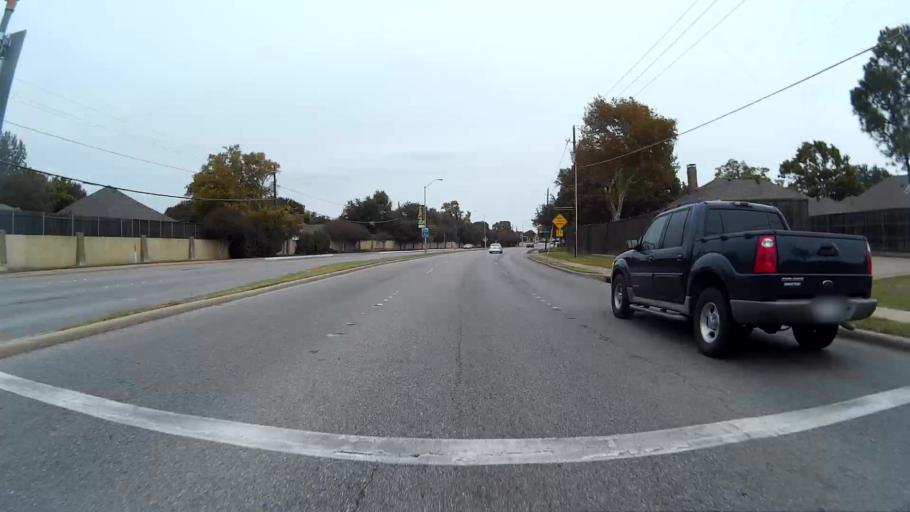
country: US
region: Texas
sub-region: Dallas County
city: Richardson
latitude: 32.9743
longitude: -96.7688
